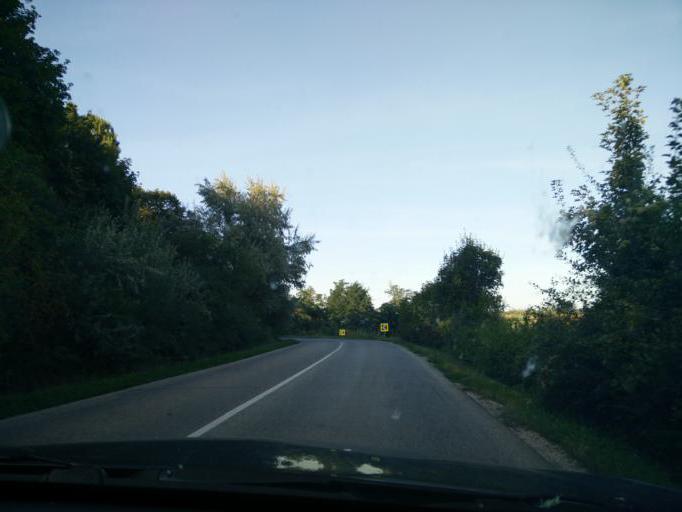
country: HU
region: Pest
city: Perbal
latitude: 47.6064
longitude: 18.7713
